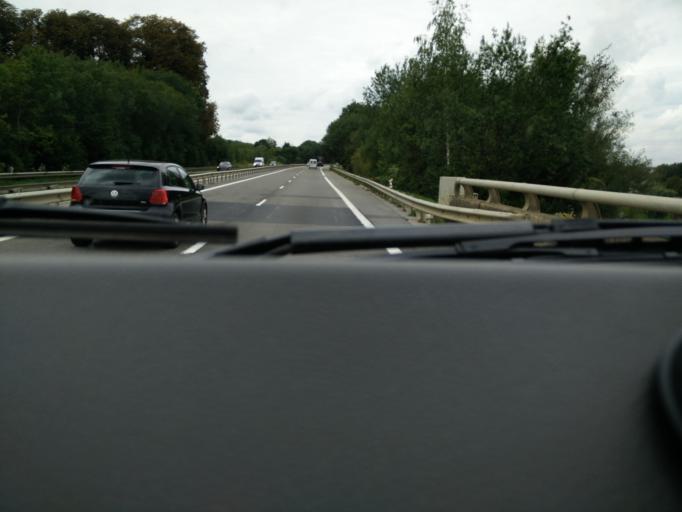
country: FR
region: Champagne-Ardenne
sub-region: Departement des Ardennes
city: Sedan
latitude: 49.6880
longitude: 4.9392
